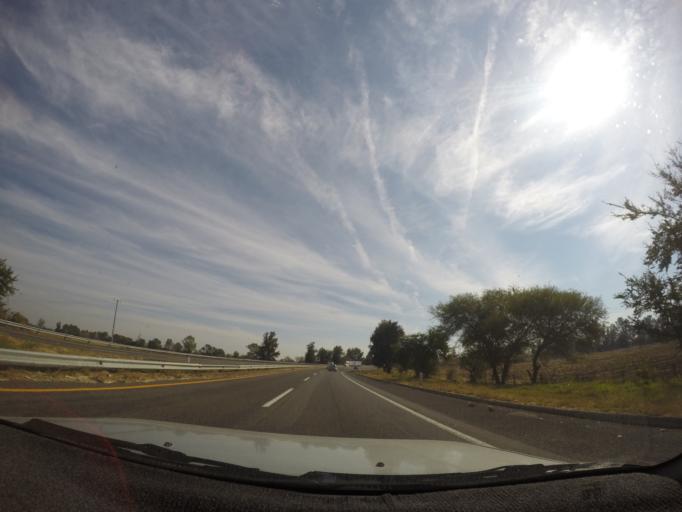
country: MX
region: Michoacan
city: Vistahermosa de Negrete
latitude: 20.2842
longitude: -102.4614
